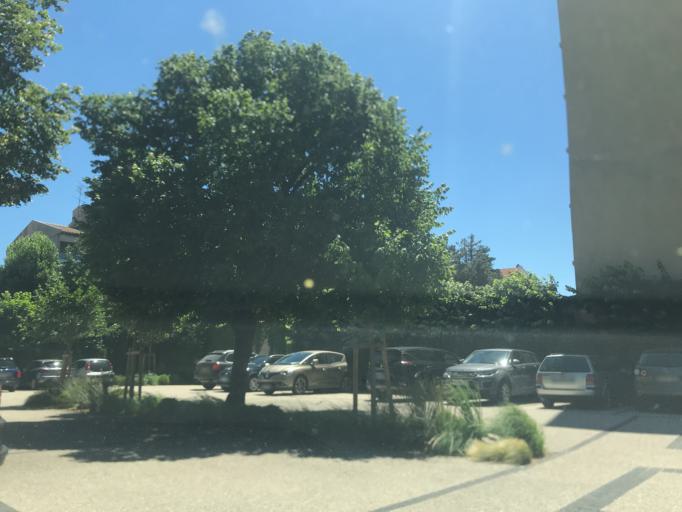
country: FR
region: Rhone-Alpes
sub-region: Departement de l'Ardeche
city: Guilherand-Granges
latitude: 44.9173
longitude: 4.8856
